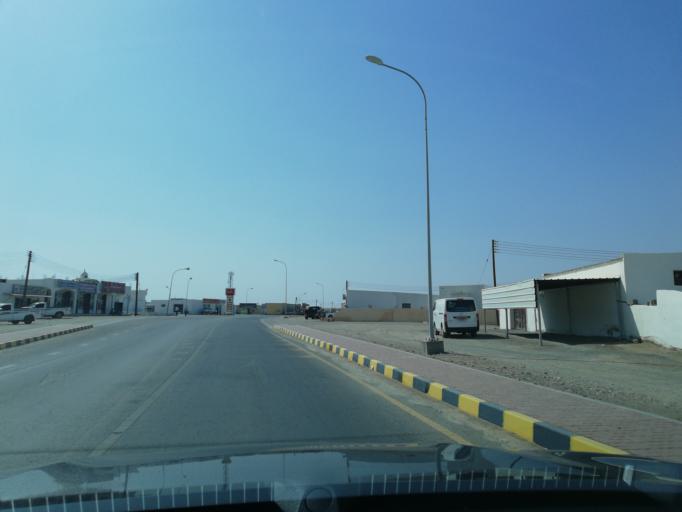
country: OM
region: Muhafazat ad Dakhiliyah
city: Adam
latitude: 22.3004
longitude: 58.0736
